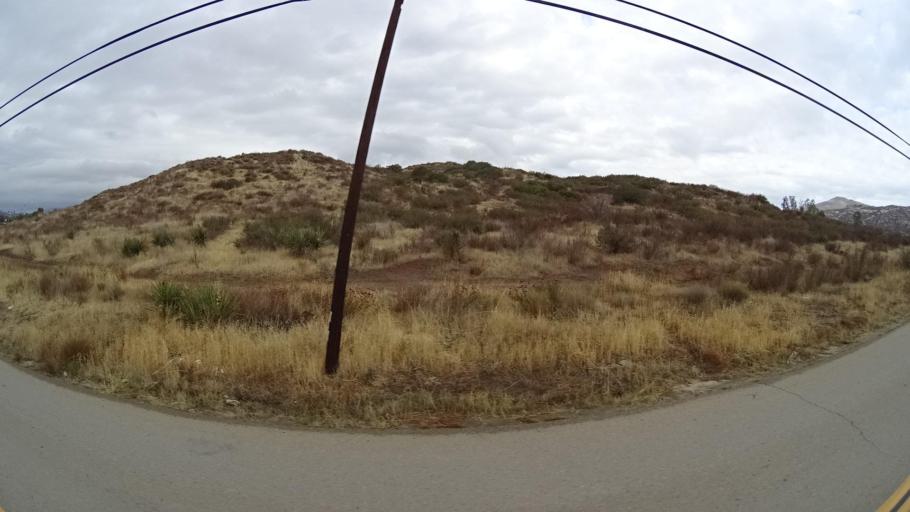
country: MX
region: Baja California
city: Tecate
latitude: 32.5792
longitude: -116.6218
